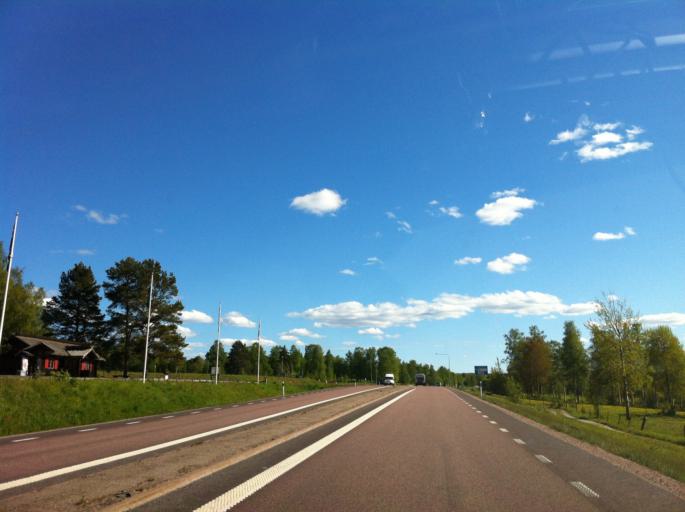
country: SE
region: Dalarna
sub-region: Rattviks Kommun
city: Raettvik
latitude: 60.8708
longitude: 15.1015
